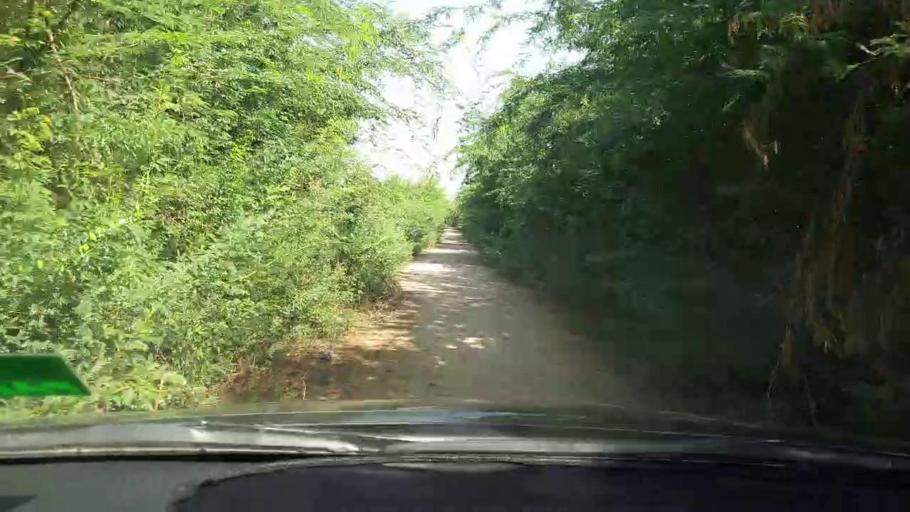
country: PK
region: Sindh
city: Tando Bago
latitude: 24.7770
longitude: 68.9459
